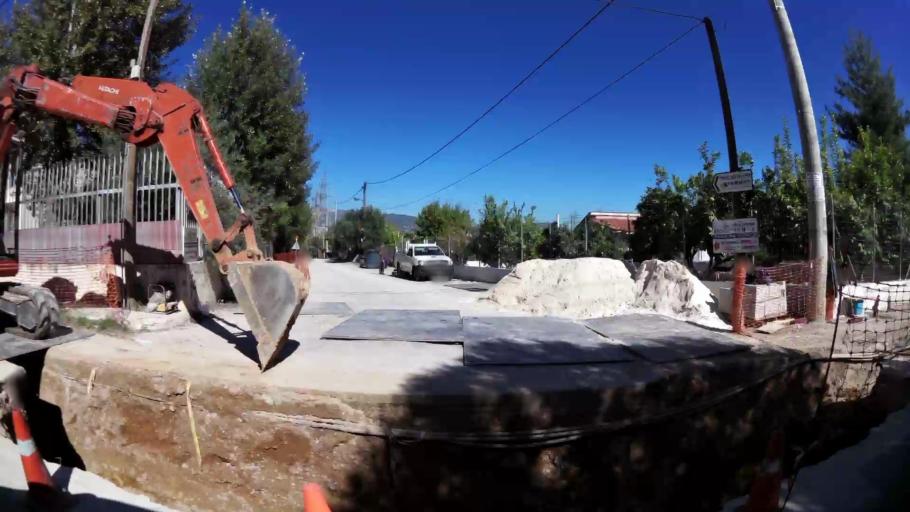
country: GR
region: Attica
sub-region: Nomarchia Anatolikis Attikis
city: Leondarion
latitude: 37.9910
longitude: 23.8531
